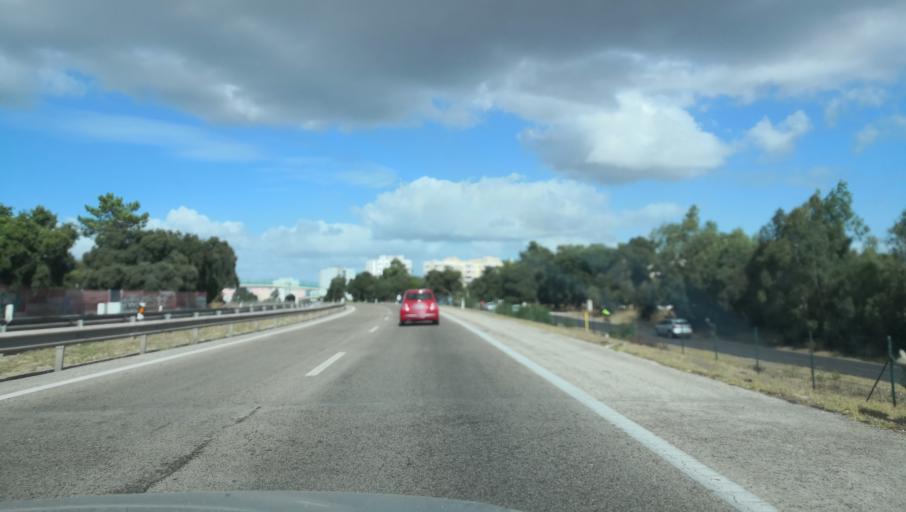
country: PT
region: Setubal
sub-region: Barreiro
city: Santo Antonio da Charneca
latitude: 38.6451
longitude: -9.0490
